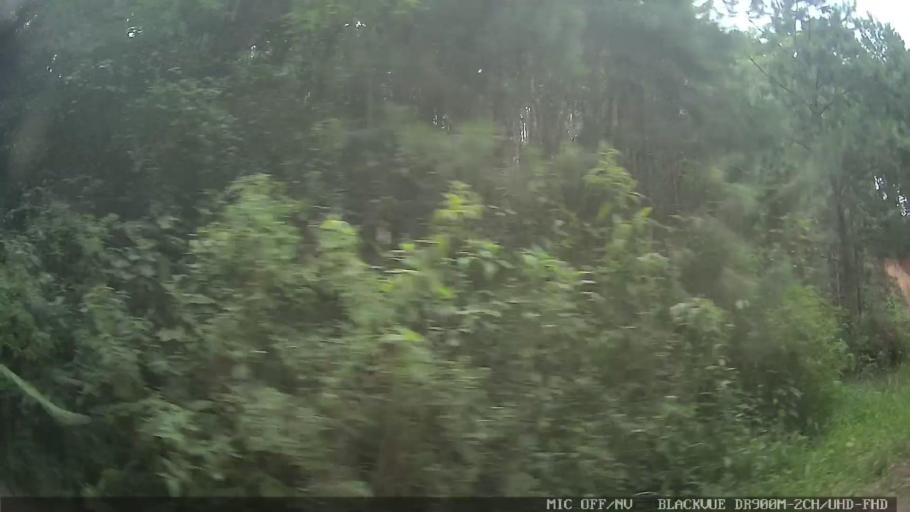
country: BR
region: Sao Paulo
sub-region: Bom Jesus Dos Perdoes
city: Bom Jesus dos Perdoes
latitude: -23.1678
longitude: -46.5118
